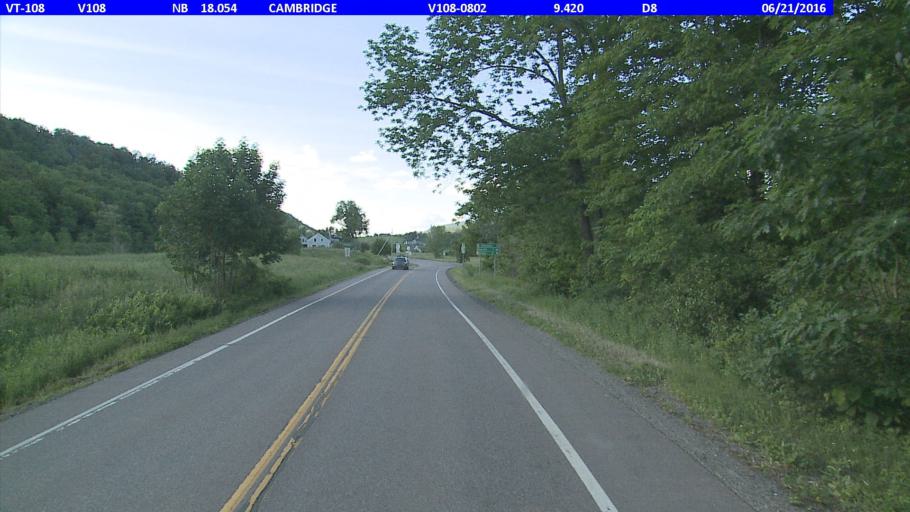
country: US
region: Vermont
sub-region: Lamoille County
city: Johnson
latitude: 44.6519
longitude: -72.8283
